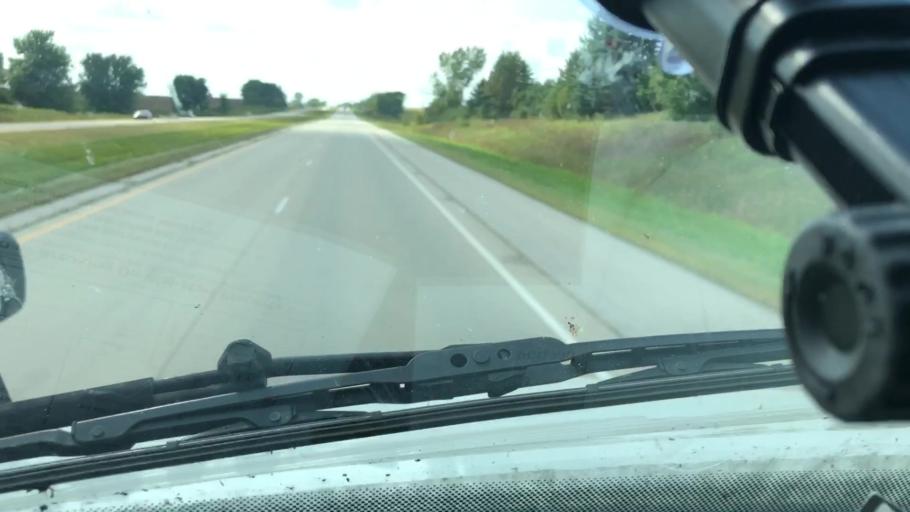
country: US
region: Minnesota
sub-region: Mower County
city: Grand Meadow
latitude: 43.7977
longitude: -92.5986
